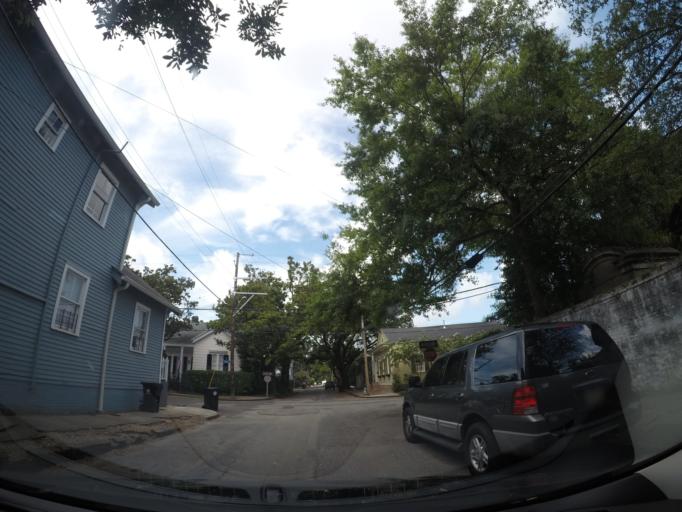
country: US
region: Louisiana
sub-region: Jefferson Parish
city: Harvey
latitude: 29.9280
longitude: -90.0853
